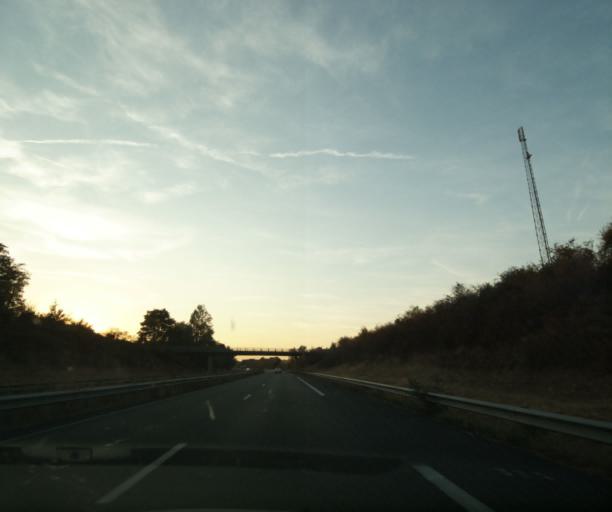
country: FR
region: Aquitaine
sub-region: Departement du Lot-et-Garonne
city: Meilhan-sur-Garonne
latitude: 44.4929
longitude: -0.0030
